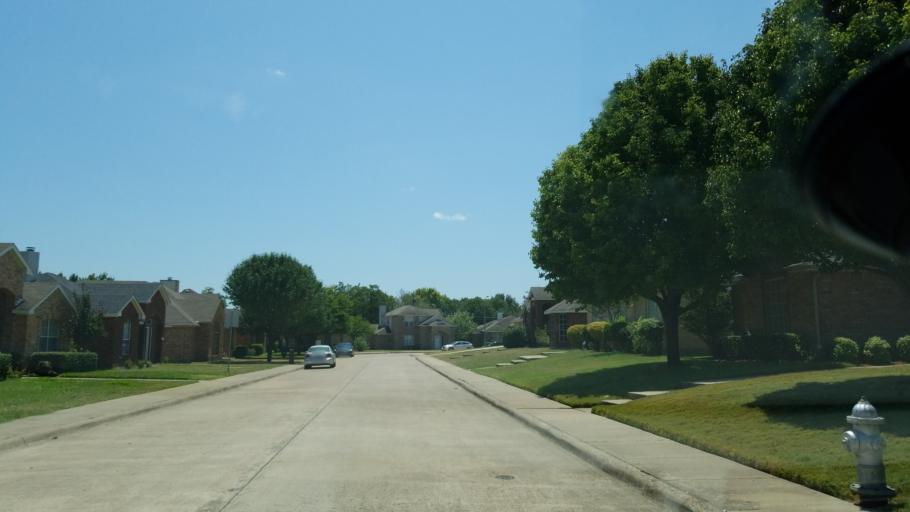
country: US
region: Texas
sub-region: Dallas County
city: Duncanville
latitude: 32.6384
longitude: -96.8841
